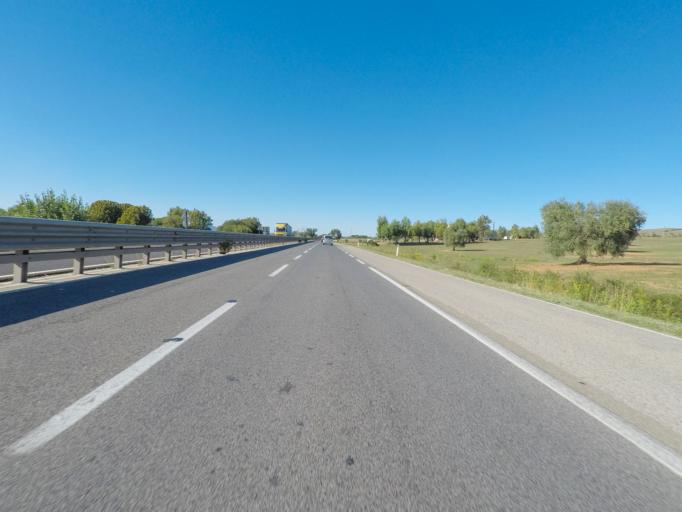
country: IT
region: Tuscany
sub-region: Provincia di Grosseto
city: Grosseto
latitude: 42.7160
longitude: 11.1431
